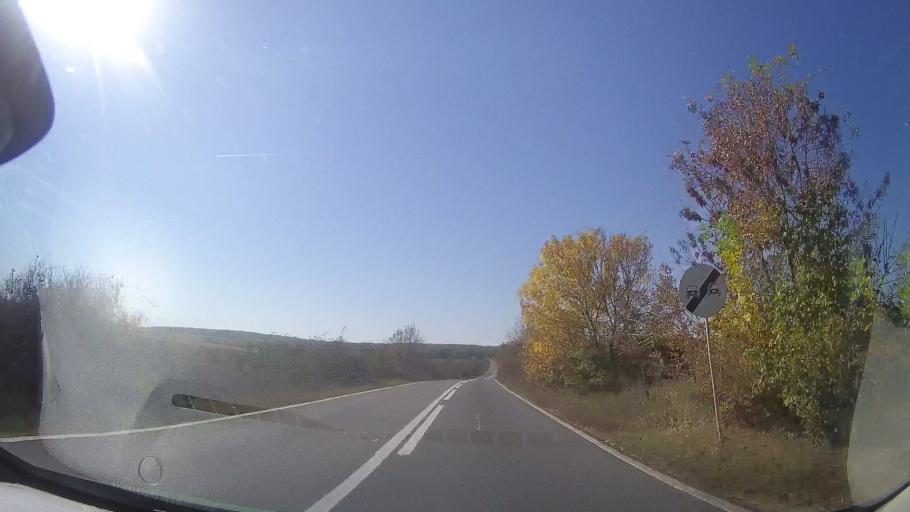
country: RO
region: Timis
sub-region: Comuna Traian Vuia
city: Traian Vuia
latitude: 45.7659
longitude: 22.0288
